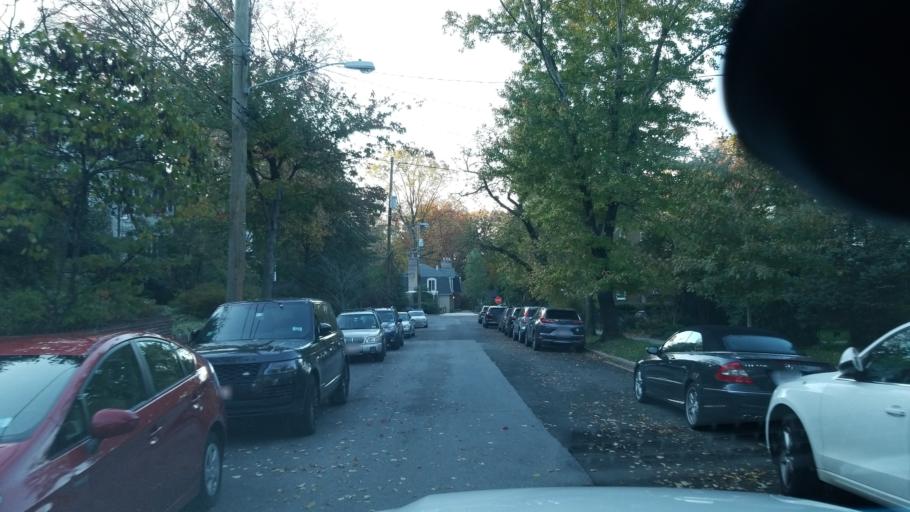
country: US
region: Maryland
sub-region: Montgomery County
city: Chevy Chase
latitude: 38.9593
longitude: -77.0575
